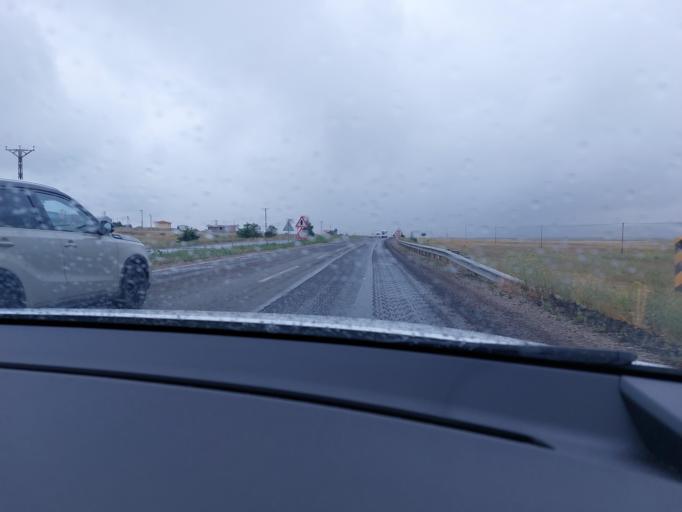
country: TR
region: Nevsehir
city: Dobada
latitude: 38.5333
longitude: 34.4435
